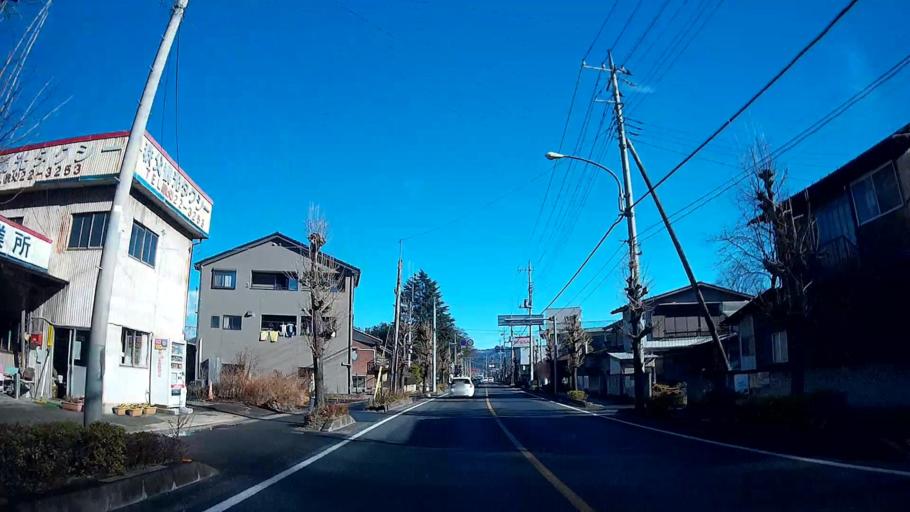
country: JP
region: Saitama
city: Chichibu
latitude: 36.0181
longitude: 139.0939
